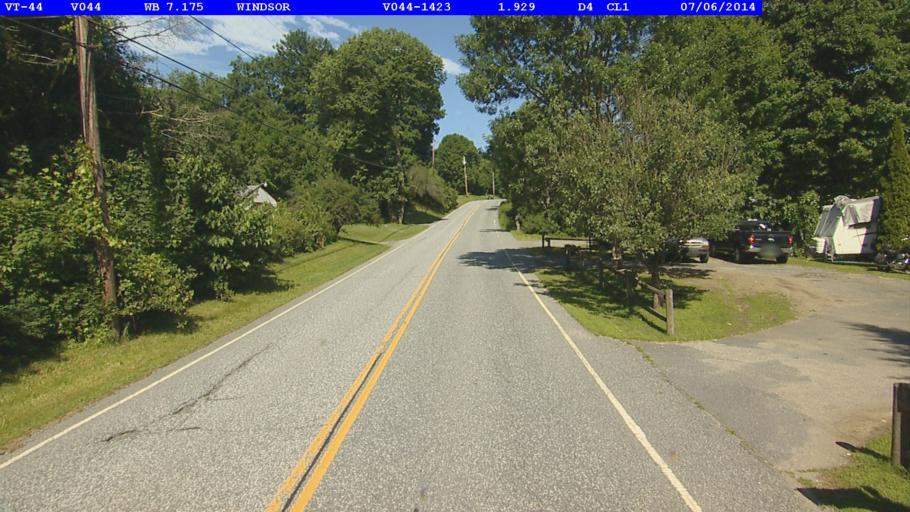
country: US
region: Vermont
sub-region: Windsor County
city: Windsor
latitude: 43.4572
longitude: -72.4185
